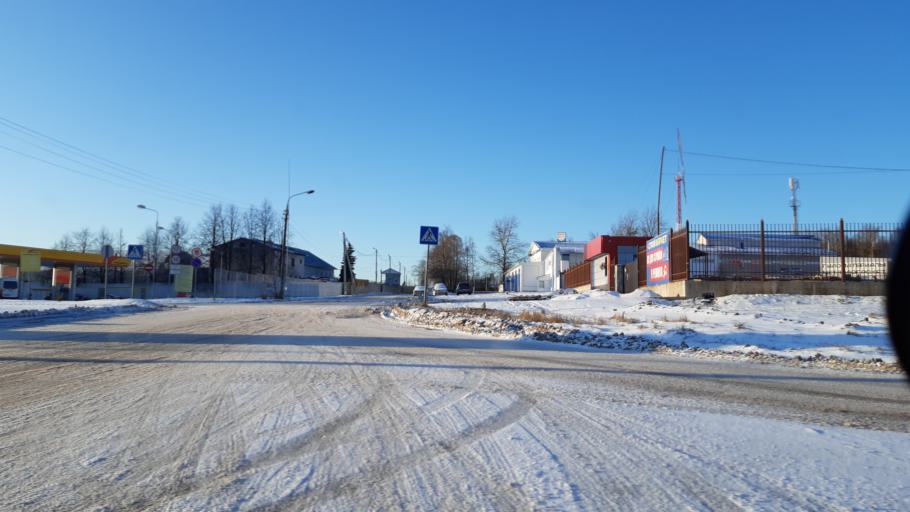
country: RU
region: Moskovskaya
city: Skoropuskovskiy
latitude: 56.3373
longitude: 38.1616
